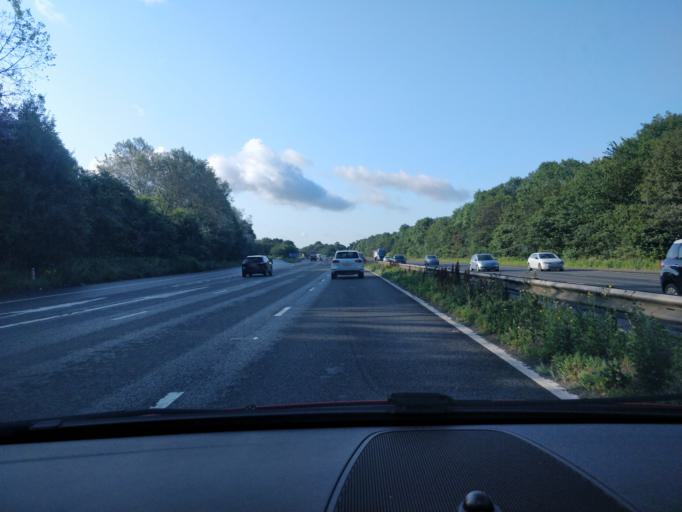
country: GB
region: England
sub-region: Knowsley
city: Knowsley
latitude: 53.4398
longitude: -2.8576
